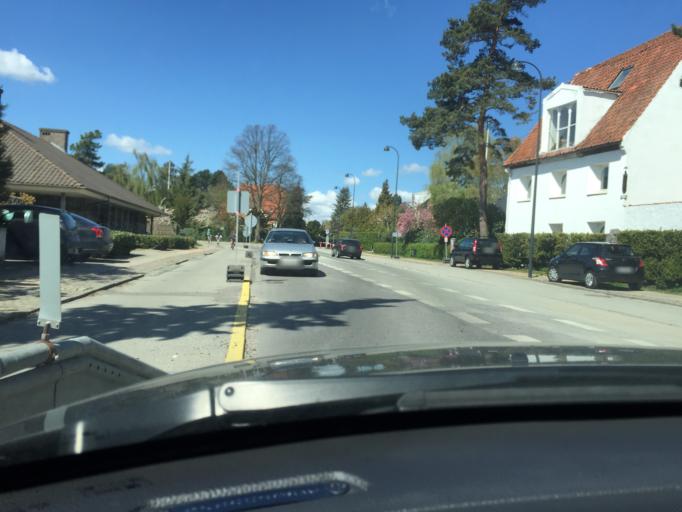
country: DK
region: Capital Region
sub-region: Gentofte Kommune
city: Charlottenlund
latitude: 55.7451
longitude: 12.5764
